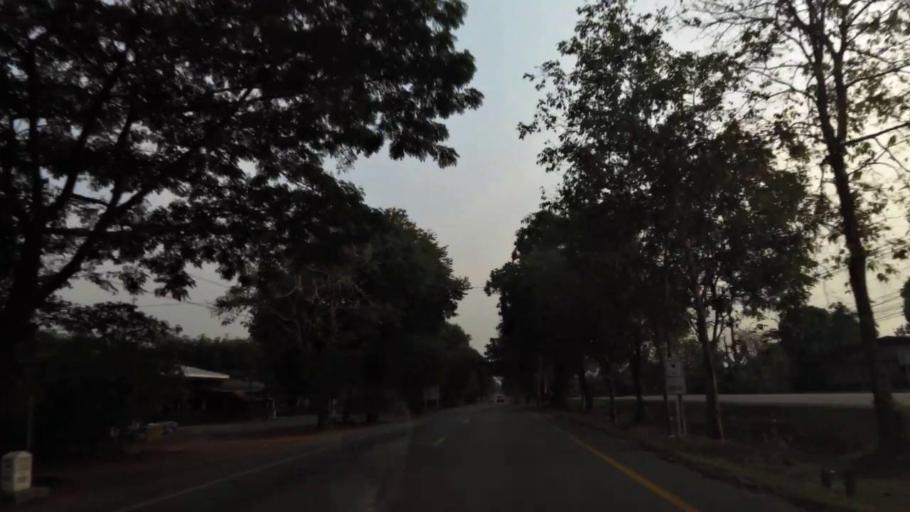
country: TH
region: Chanthaburi
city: Khlung
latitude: 12.4949
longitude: 102.1728
